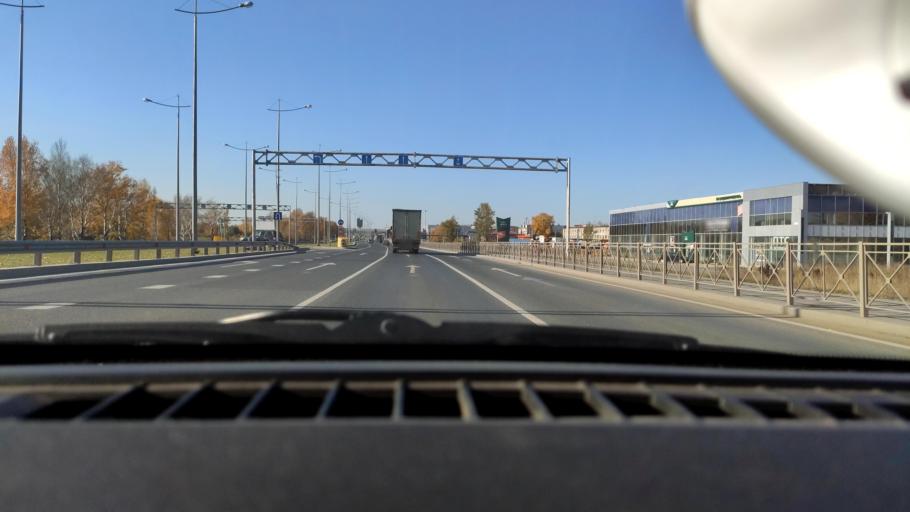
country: RU
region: Perm
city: Kondratovo
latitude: 57.9488
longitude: 56.0905
